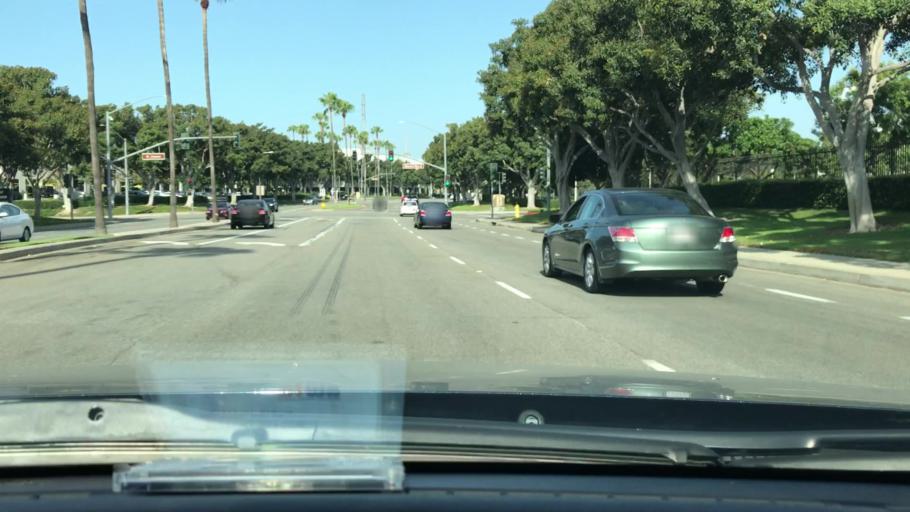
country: US
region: California
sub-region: Orange County
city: Irvine
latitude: 33.6572
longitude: -117.7658
